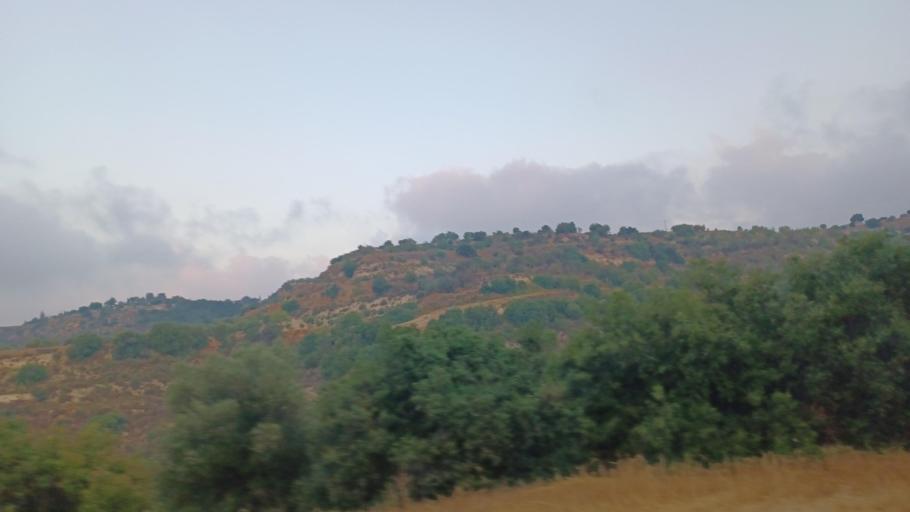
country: CY
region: Pafos
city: Mesogi
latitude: 34.8090
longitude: 32.5745
